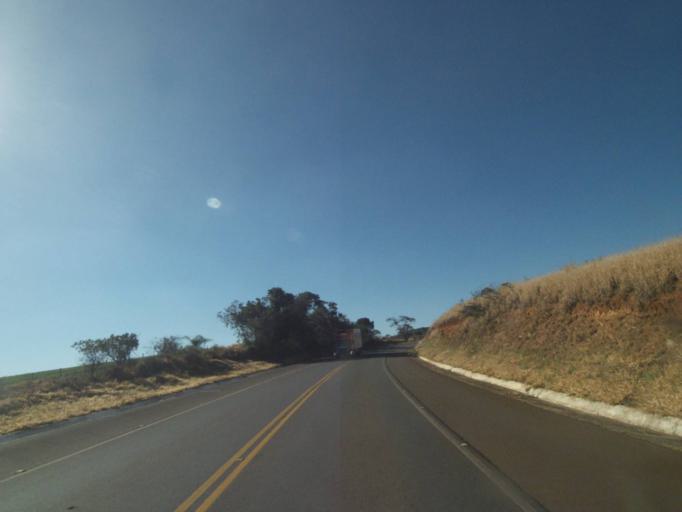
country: BR
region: Parana
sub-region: Tibagi
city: Tibagi
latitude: -24.7400
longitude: -50.4591
